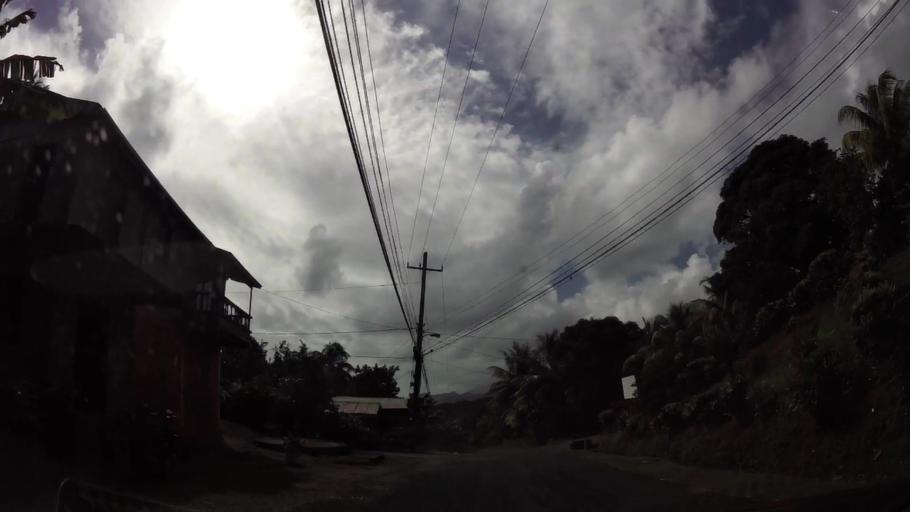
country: DM
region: Saint David
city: Castle Bruce
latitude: 15.4672
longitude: -61.2481
